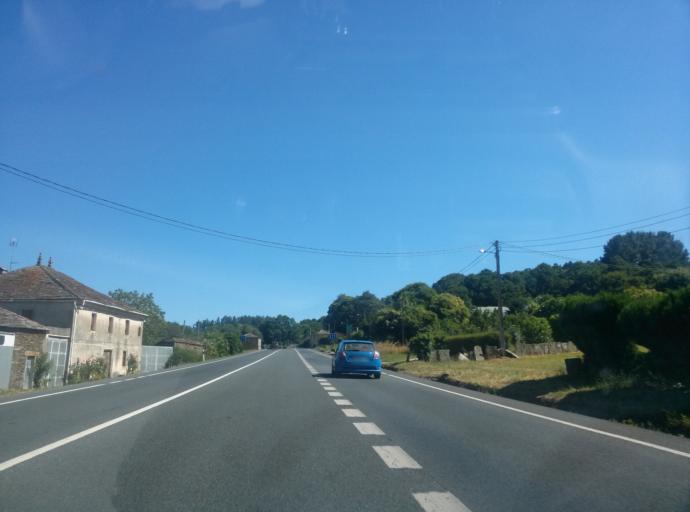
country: ES
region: Galicia
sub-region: Provincia de Lugo
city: Outeiro de Rei
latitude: 43.0550
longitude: -7.5971
